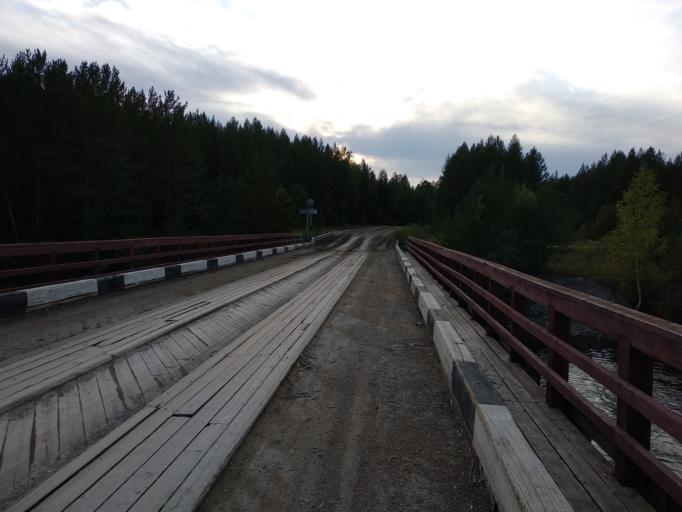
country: RU
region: Sverdlovsk
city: Cheremukhovo
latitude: 60.3891
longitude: 59.9040
